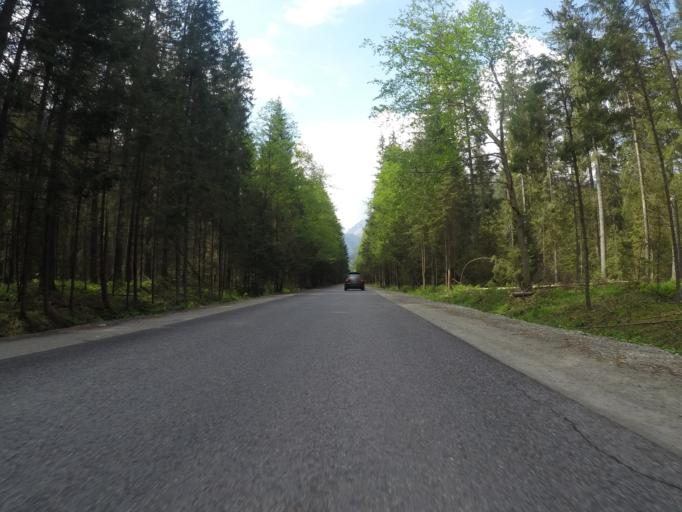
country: PL
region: Lesser Poland Voivodeship
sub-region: Powiat tatrzanski
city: Bukowina Tatrzanska
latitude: 49.2582
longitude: 20.1061
